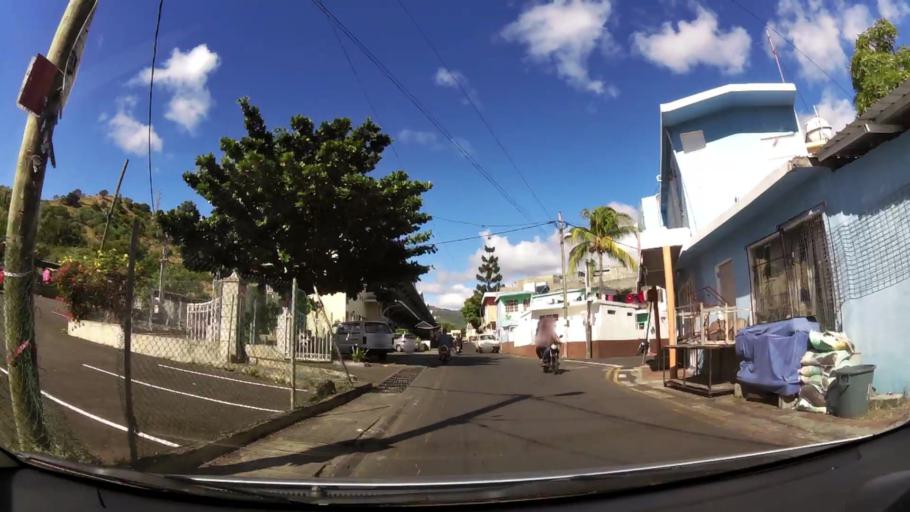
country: MU
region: Pamplemousses
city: Le Hochet
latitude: -20.1548
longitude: 57.5196
